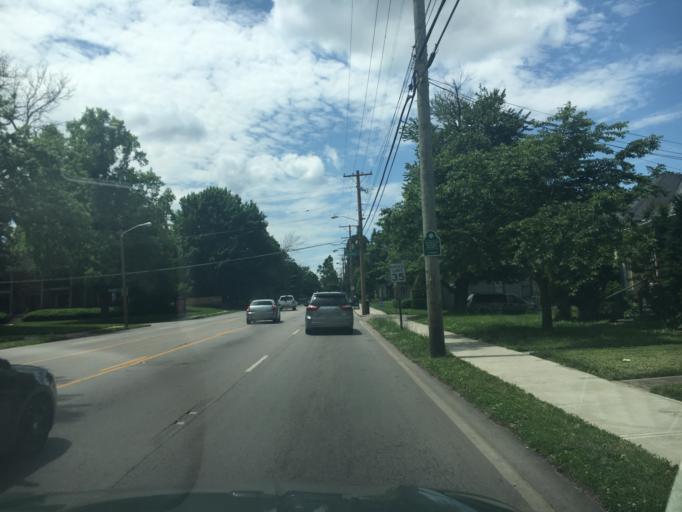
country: US
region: Kentucky
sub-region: Fayette County
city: Lexington-Fayette
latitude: 38.0577
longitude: -84.4875
